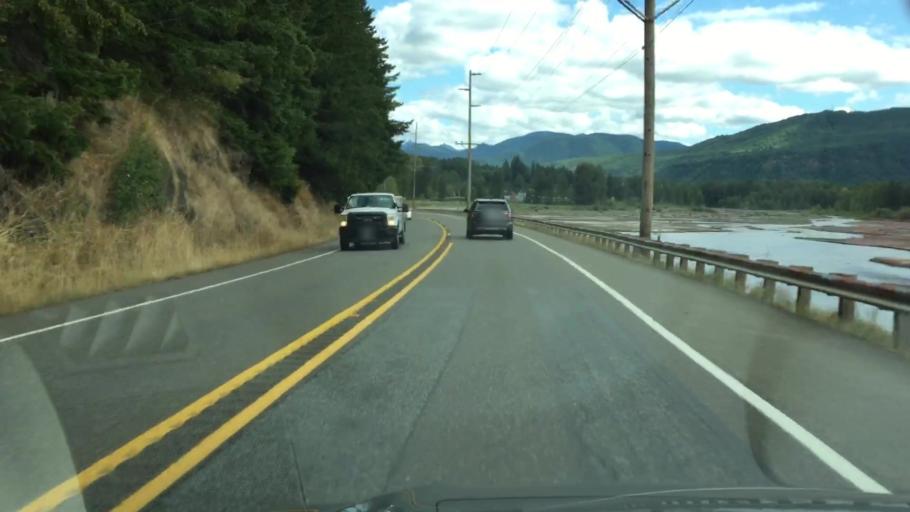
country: US
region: Washington
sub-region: Pierce County
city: Eatonville
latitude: 46.7703
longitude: -122.2077
